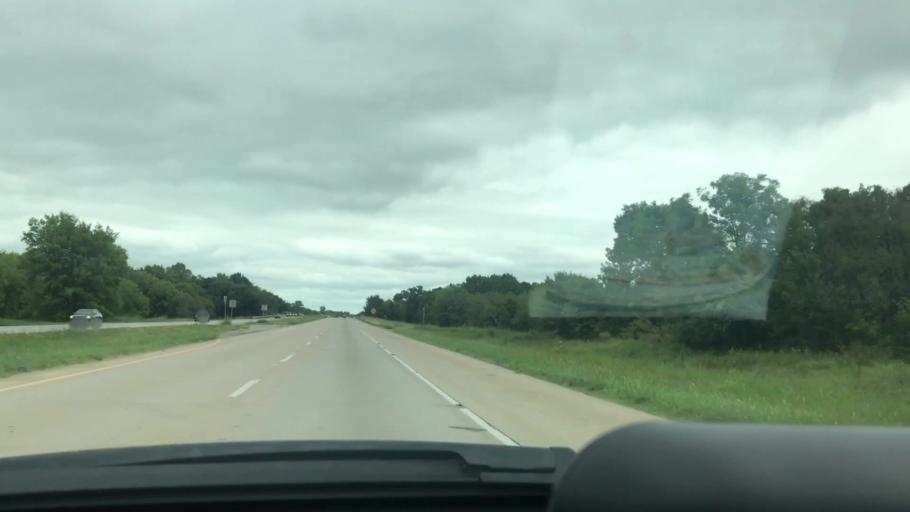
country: US
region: Oklahoma
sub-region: Mayes County
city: Chouteau
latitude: 36.2033
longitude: -95.3408
